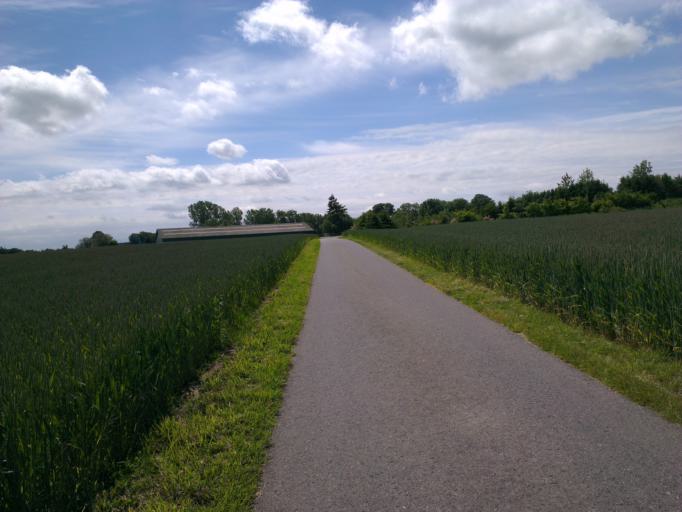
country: DK
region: Capital Region
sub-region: Frederikssund Kommune
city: Skibby
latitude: 55.7901
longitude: 11.9893
